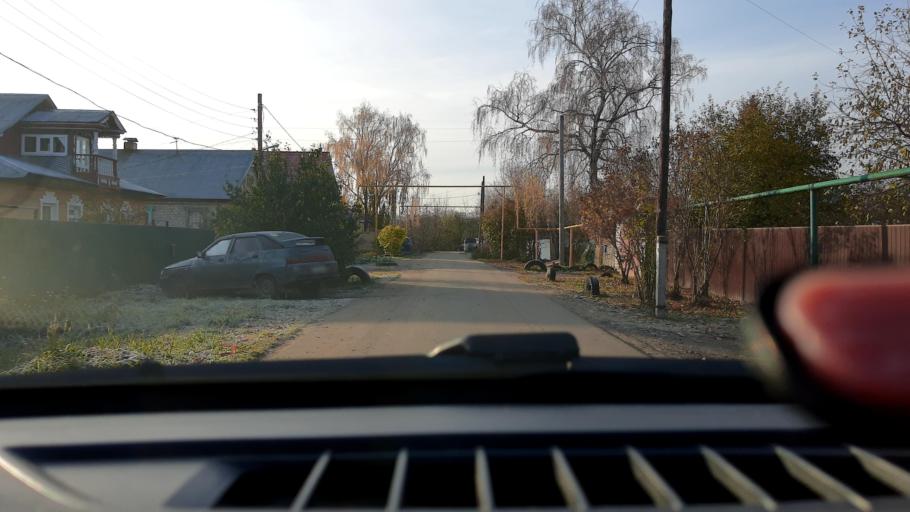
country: RU
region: Nizjnij Novgorod
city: Nizhniy Novgorod
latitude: 56.2721
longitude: 43.9528
